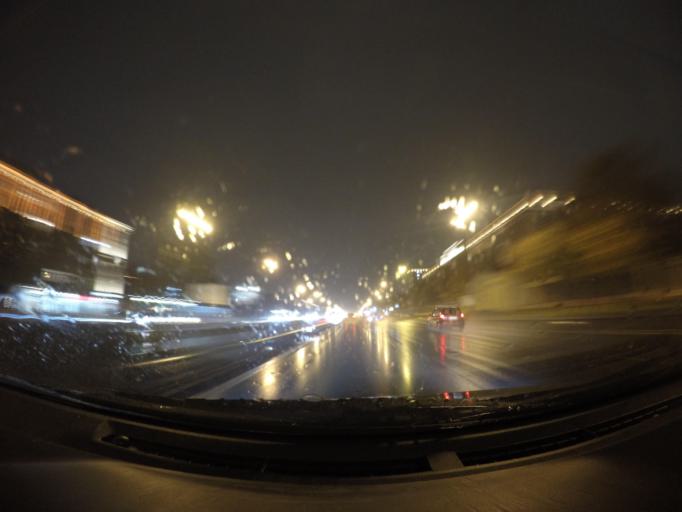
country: RU
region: Moscow
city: Kolomenskoye
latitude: 55.6462
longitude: 37.6706
